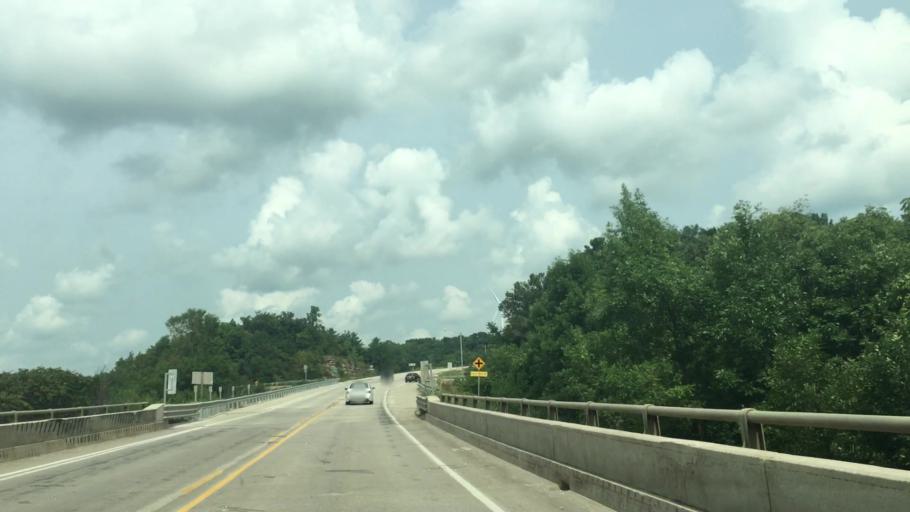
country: US
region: Iowa
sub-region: Winneshiek County
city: Decorah
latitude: 43.2989
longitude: -91.8120
